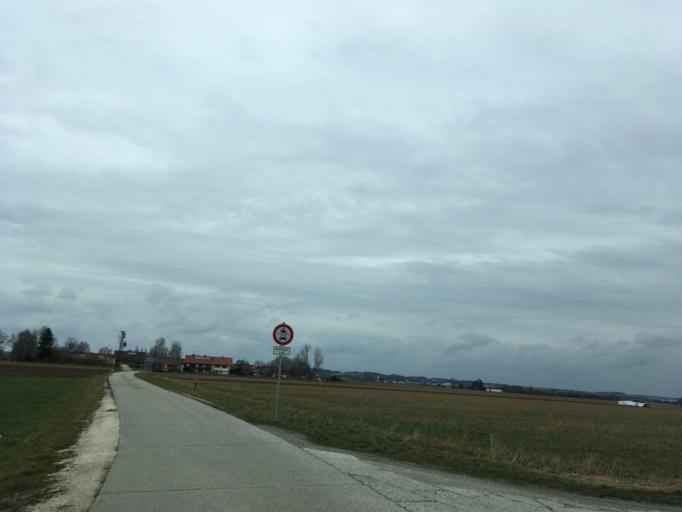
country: DE
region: Bavaria
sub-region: Upper Bavaria
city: Ampfing
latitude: 48.2346
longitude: 12.4012
